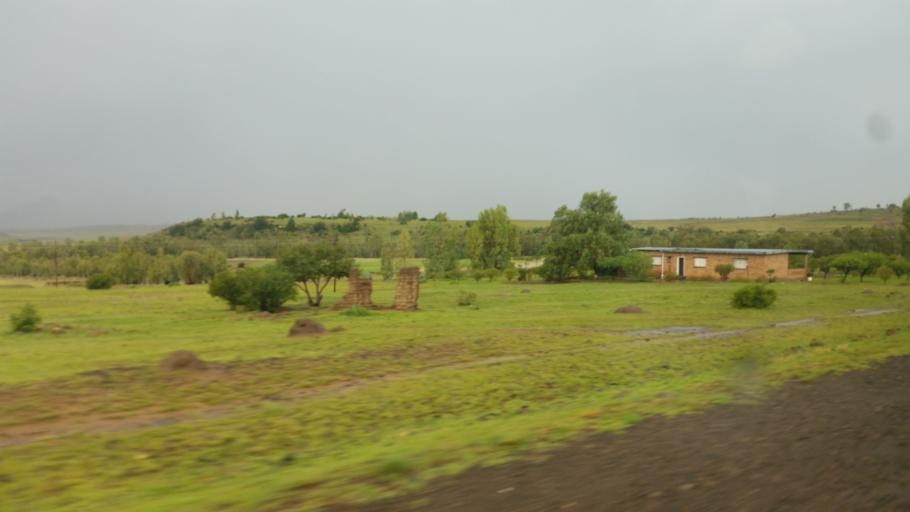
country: LS
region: Mafeteng
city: Mafeteng
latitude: -29.7541
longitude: 27.1652
